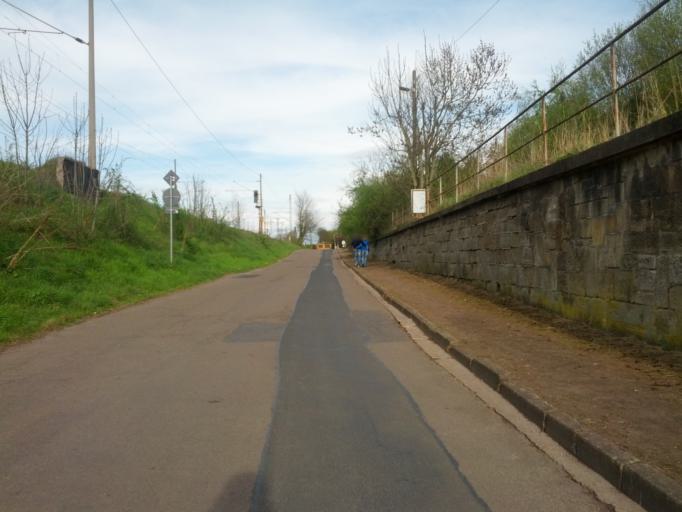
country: DE
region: Thuringia
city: Eisenach
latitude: 50.9783
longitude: 10.2981
